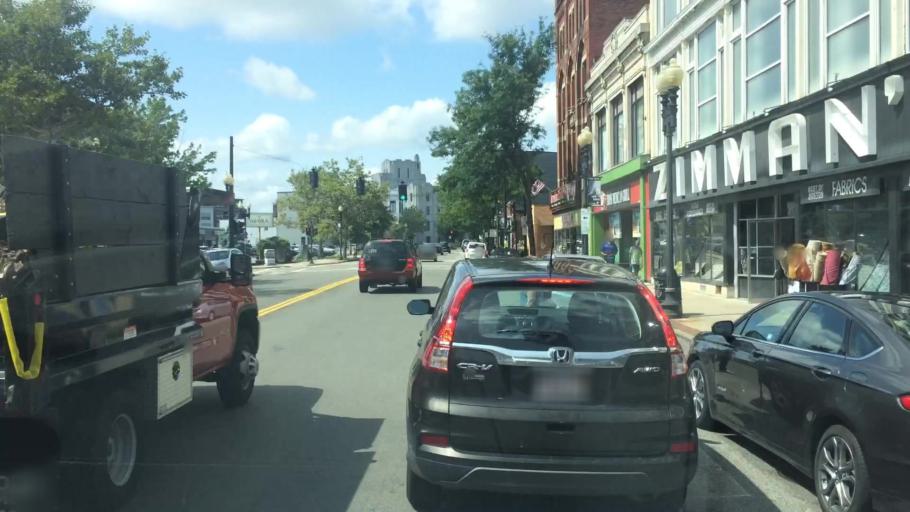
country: US
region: Massachusetts
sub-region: Essex County
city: Lynn
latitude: 42.4629
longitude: -70.9488
